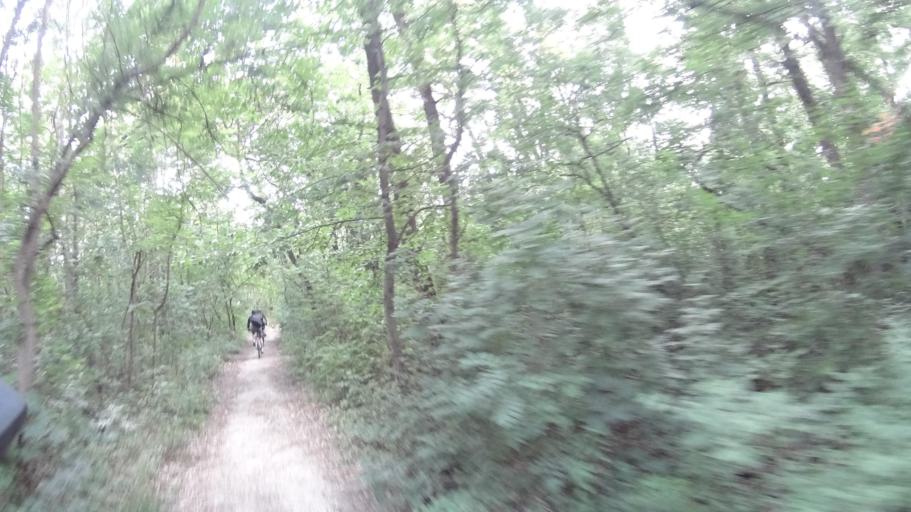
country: HU
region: Pest
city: Budakeszi
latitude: 47.4940
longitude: 18.9476
